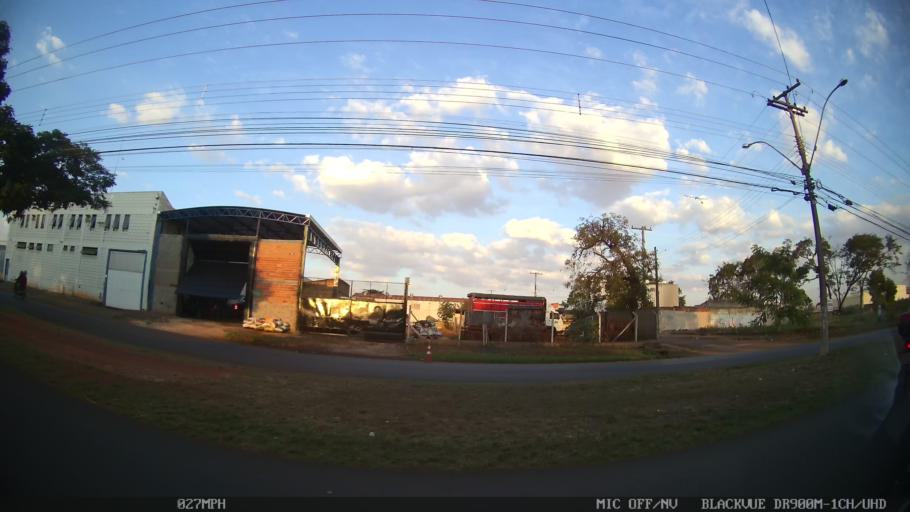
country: BR
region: Sao Paulo
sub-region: Ribeirao Preto
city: Ribeirao Preto
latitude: -21.1516
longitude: -47.7675
